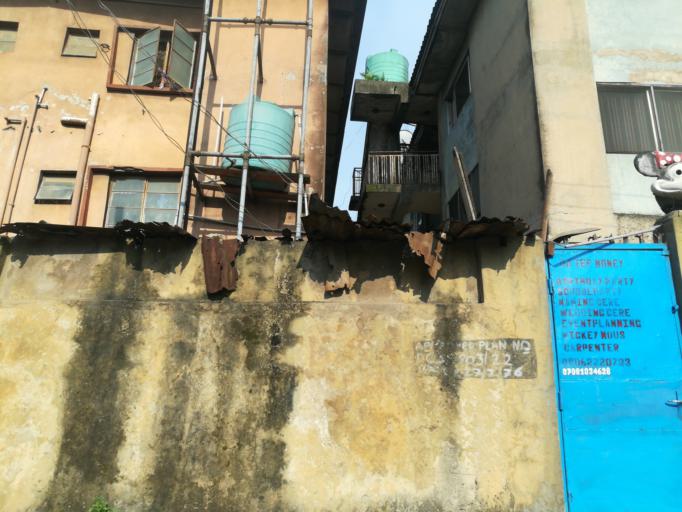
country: NG
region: Lagos
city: Ojota
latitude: 6.5950
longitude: 3.4000
